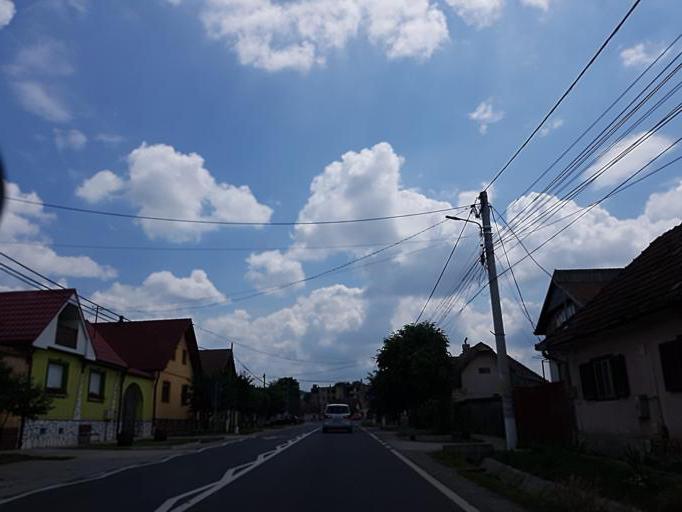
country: RO
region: Sibiu
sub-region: Comuna Slimnic
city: Slimnic
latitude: 45.9643
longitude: 24.1623
